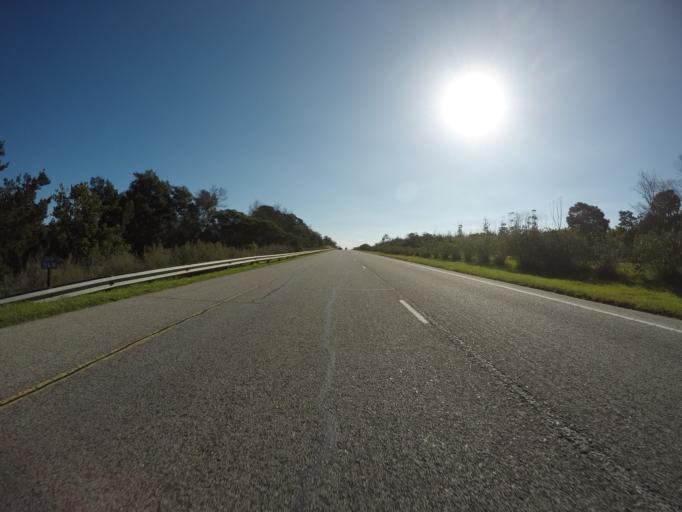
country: ZA
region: Eastern Cape
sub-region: Nelson Mandela Bay Metropolitan Municipality
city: Uitenhage
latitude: -33.9418
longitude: 25.3855
